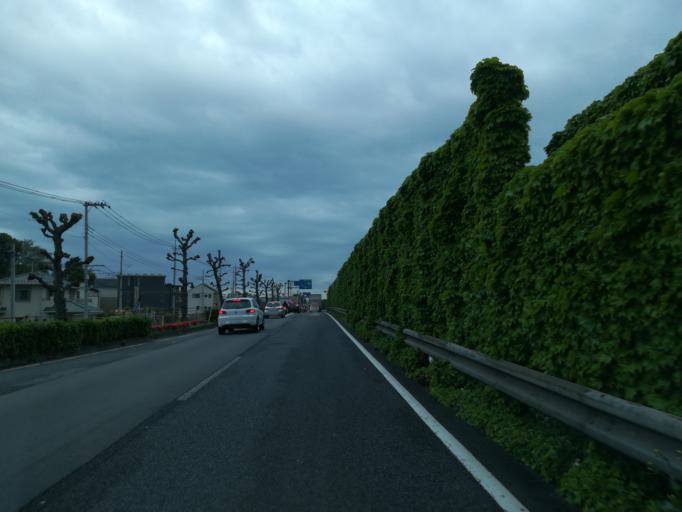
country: JP
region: Saitama
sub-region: Kawaguchi-shi
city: Hatogaya-honcho
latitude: 35.8885
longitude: 139.7237
